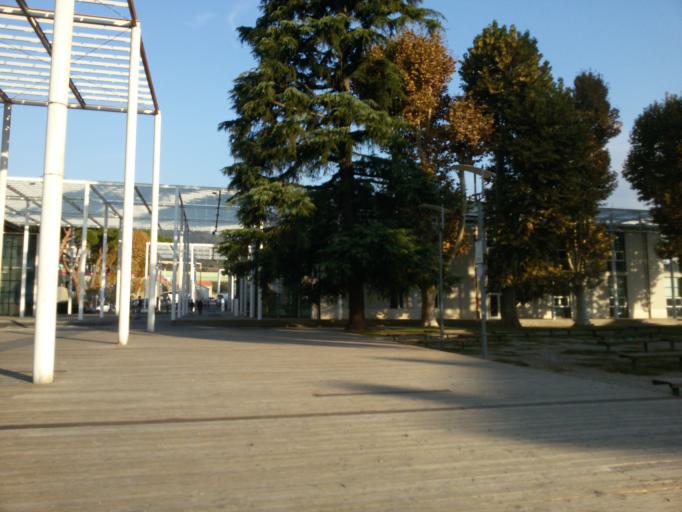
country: IT
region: Liguria
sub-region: Provincia di Savona
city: Savona
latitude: 44.2992
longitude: 8.4519
